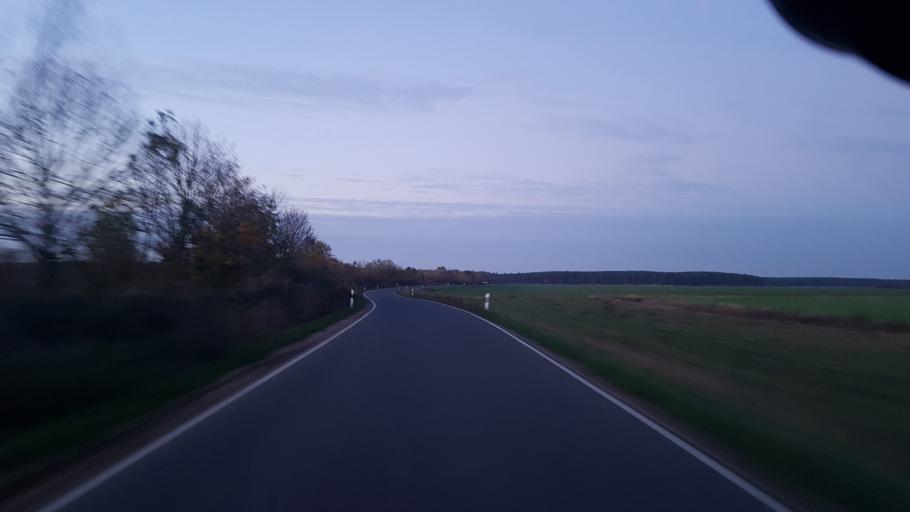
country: DE
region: Saxony
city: Arzberg
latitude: 51.5426
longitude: 13.1354
